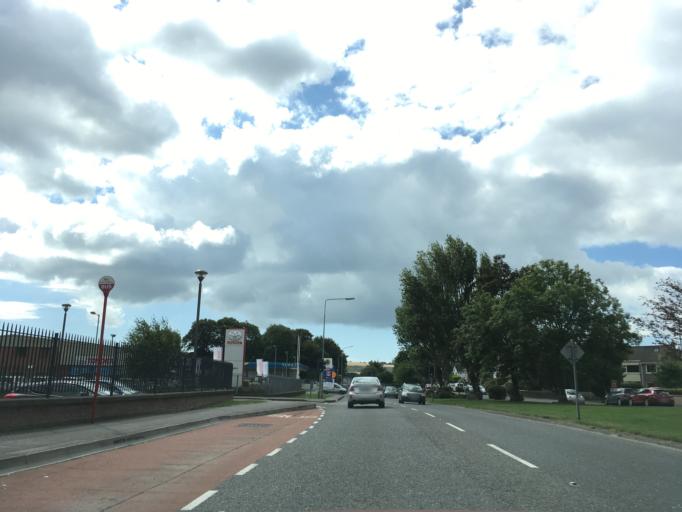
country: IE
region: Munster
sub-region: County Cork
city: Carrigaline
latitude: 51.8211
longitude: -8.3924
